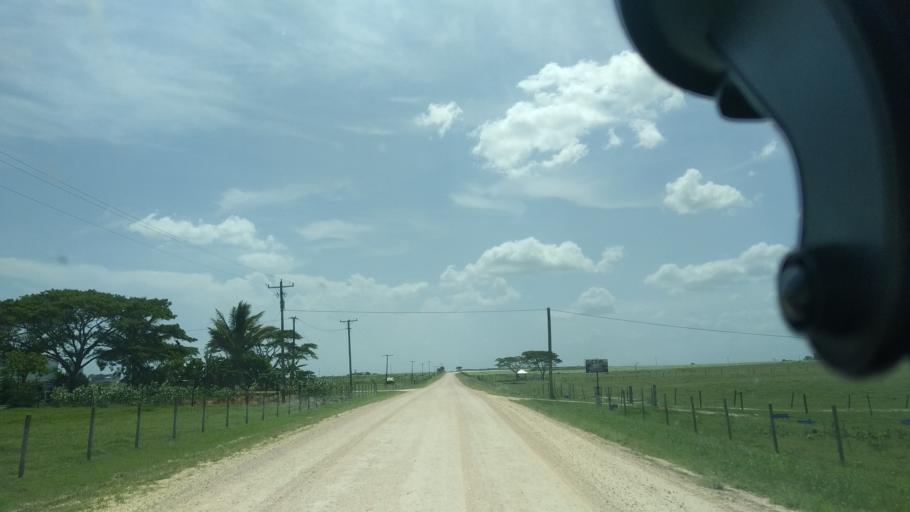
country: BZ
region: Cayo
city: San Ignacio
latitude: 17.3148
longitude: -89.0407
